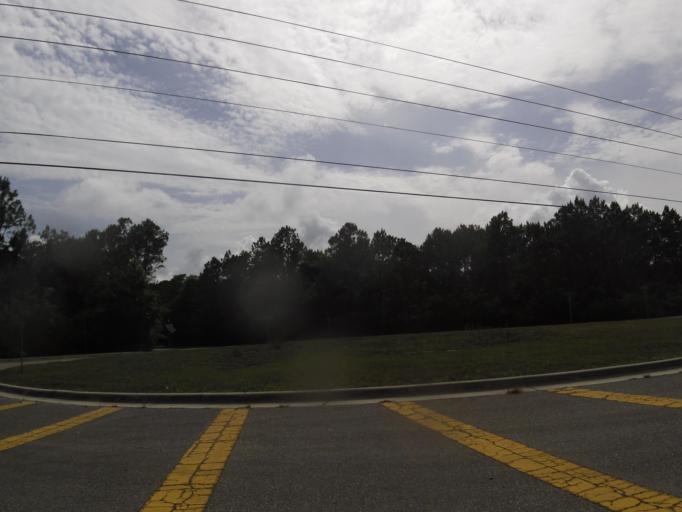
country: US
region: Florida
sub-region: Saint Johns County
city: Saint Augustine
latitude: 29.8981
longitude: -81.3462
